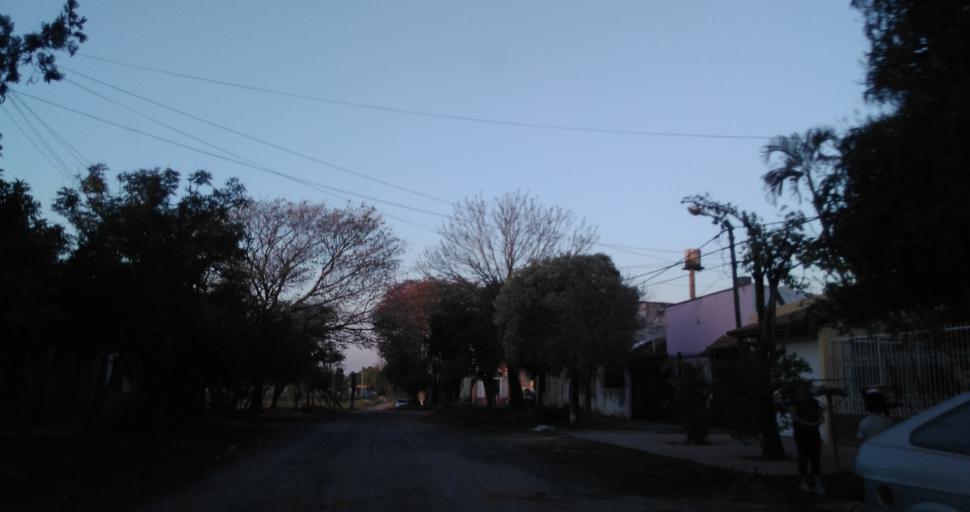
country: AR
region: Chaco
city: Resistencia
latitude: -27.4549
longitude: -58.9728
